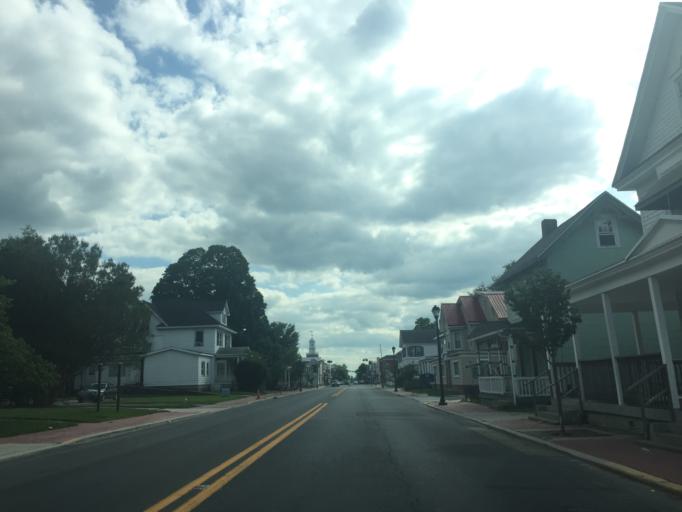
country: US
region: Delaware
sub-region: Sussex County
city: Georgetown
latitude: 38.6928
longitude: -75.3824
